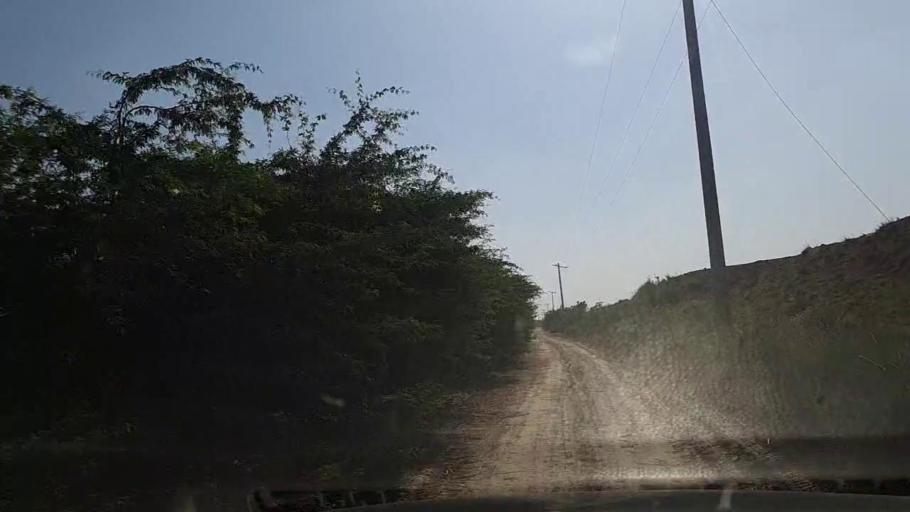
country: PK
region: Sindh
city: Daro Mehar
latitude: 24.7774
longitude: 68.0689
